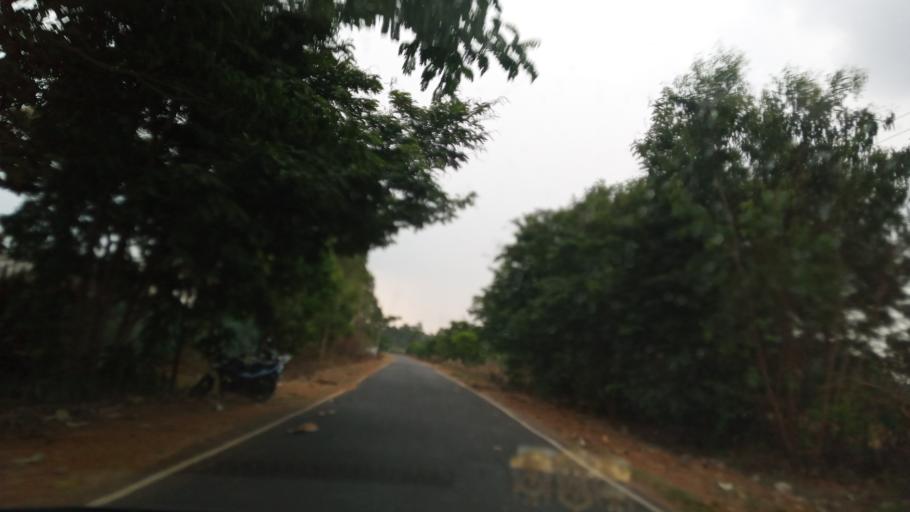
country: IN
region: Karnataka
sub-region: Kolar
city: Mulbagal
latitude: 13.1240
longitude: 78.3477
